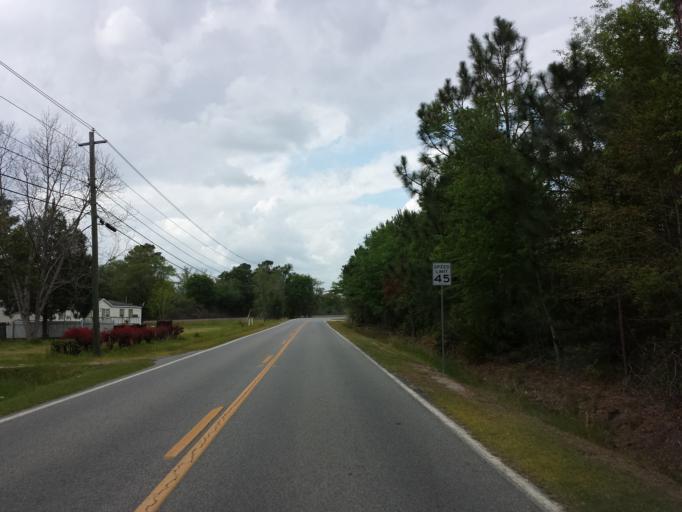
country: US
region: Georgia
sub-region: Lowndes County
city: Hahira
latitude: 31.0396
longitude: -83.3899
